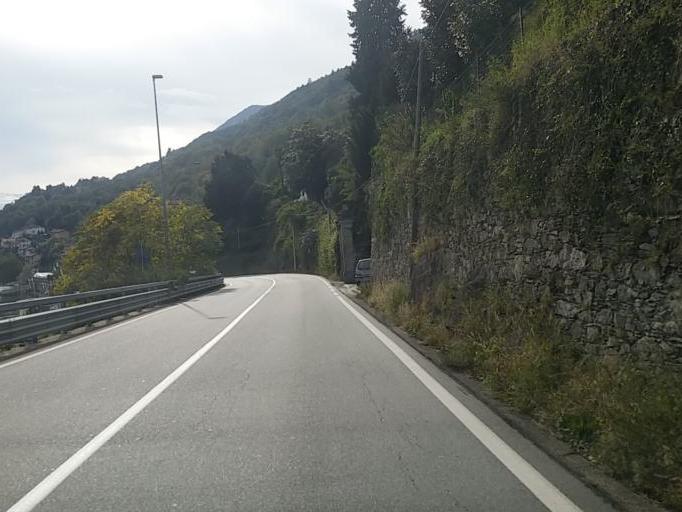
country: IT
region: Piedmont
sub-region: Provincia Verbano-Cusio-Ossola
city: Gonte
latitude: 46.0081
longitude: 8.6625
